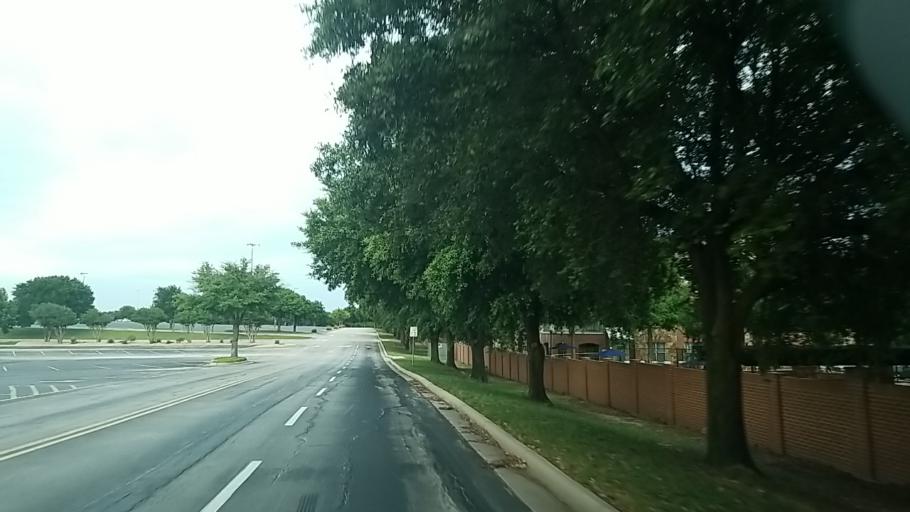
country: US
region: Texas
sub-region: Denton County
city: Lewisville
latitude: 32.9999
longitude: -96.9728
